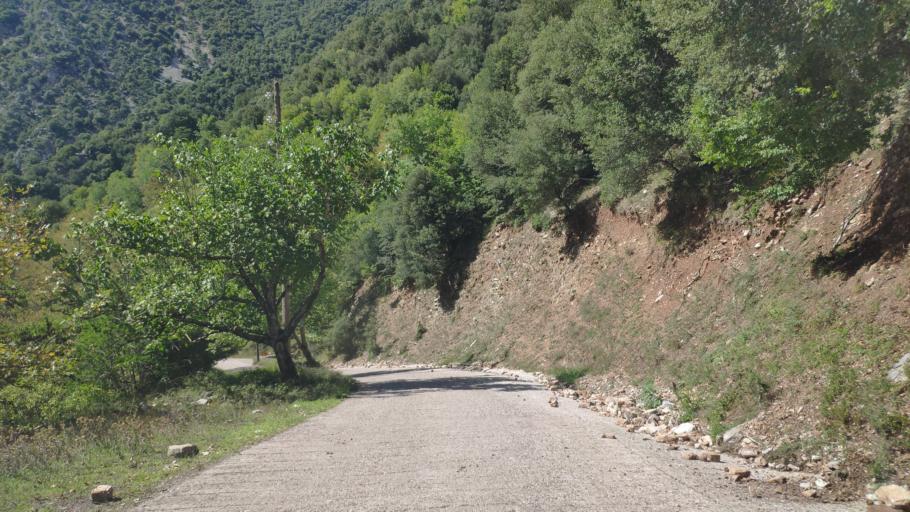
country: GR
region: Central Greece
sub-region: Nomos Evrytanias
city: Kerasochori
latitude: 39.1374
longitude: 21.6438
